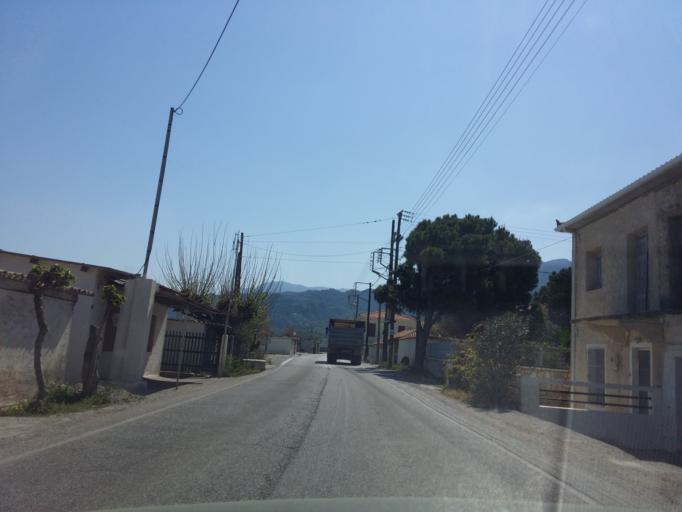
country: GR
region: West Greece
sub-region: Nomos Achaias
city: Aiyira
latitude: 38.1406
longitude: 22.3835
